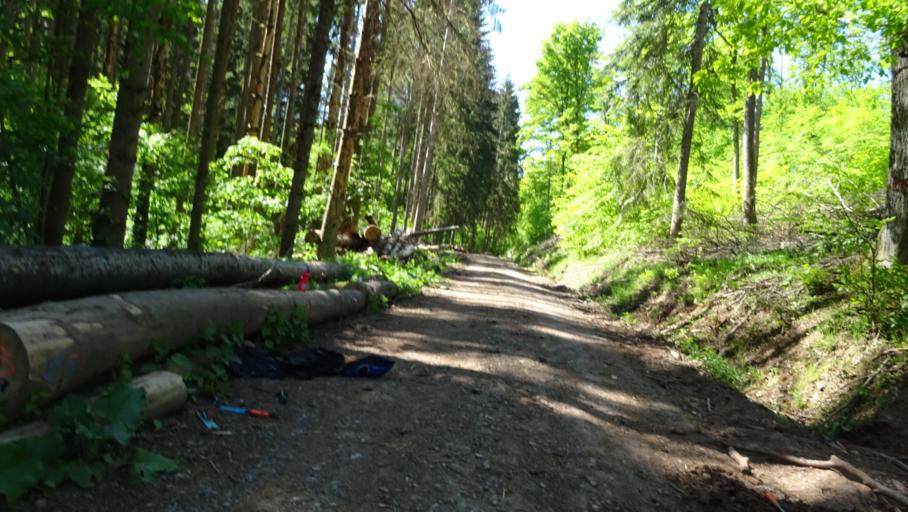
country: DE
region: Baden-Wuerttemberg
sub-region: Karlsruhe Region
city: Limbach
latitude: 49.4127
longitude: 9.2355
